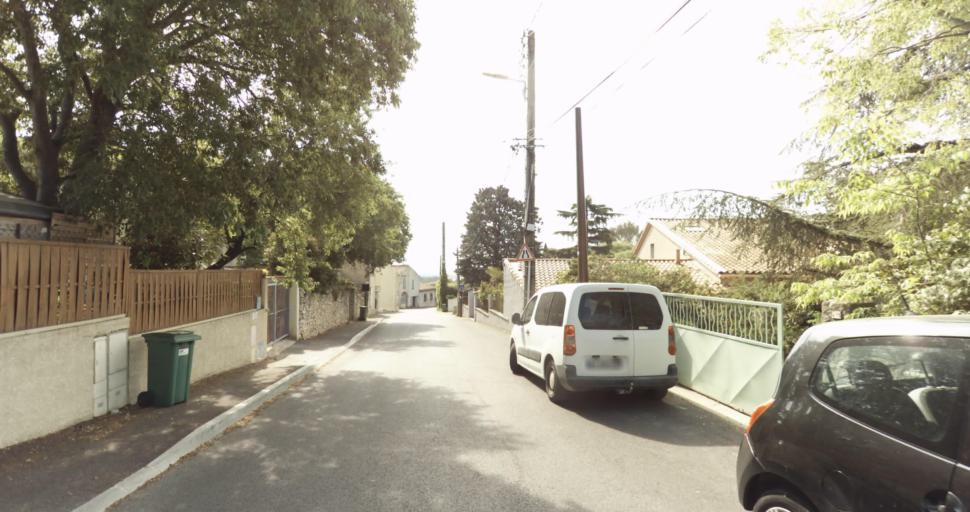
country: FR
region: Languedoc-Roussillon
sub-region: Departement du Gard
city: Poulx
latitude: 43.8659
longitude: 4.3981
